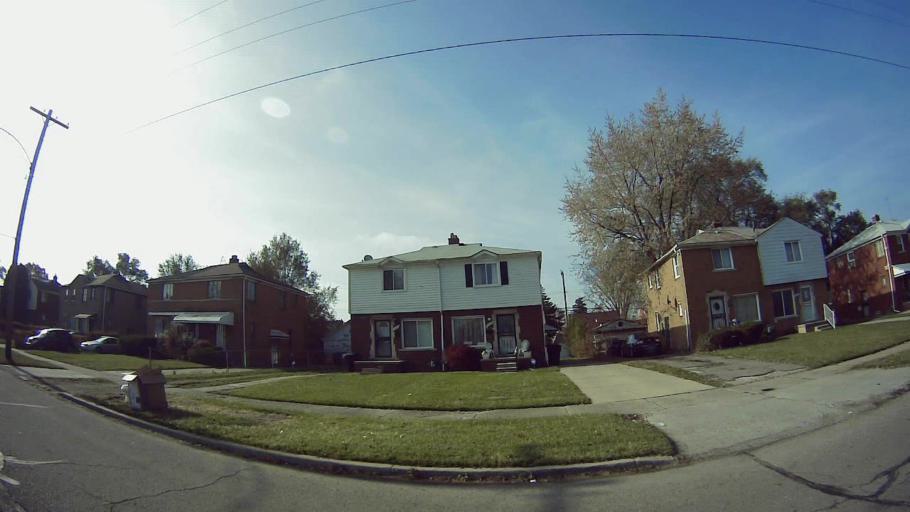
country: US
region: Michigan
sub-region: Oakland County
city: Oak Park
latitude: 42.4287
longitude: -83.1804
